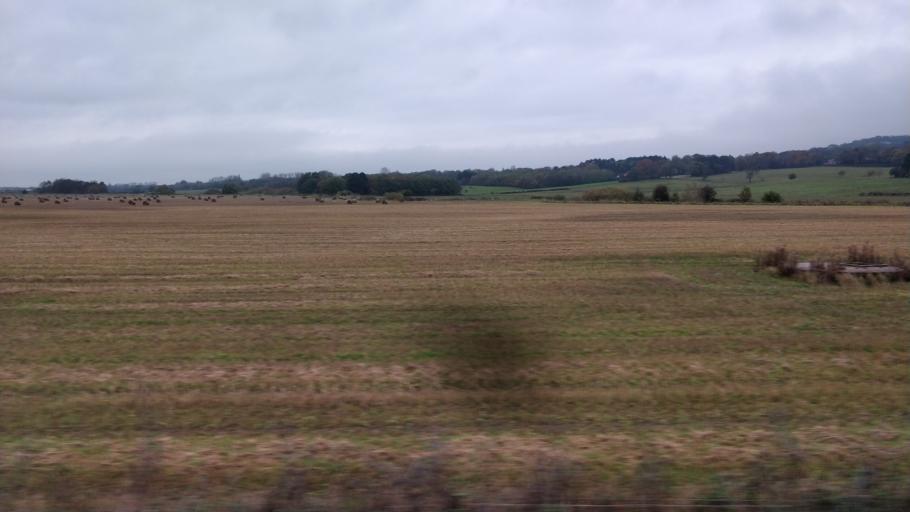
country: GB
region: England
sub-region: Lancashire
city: Parbold
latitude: 53.5925
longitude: -2.7787
